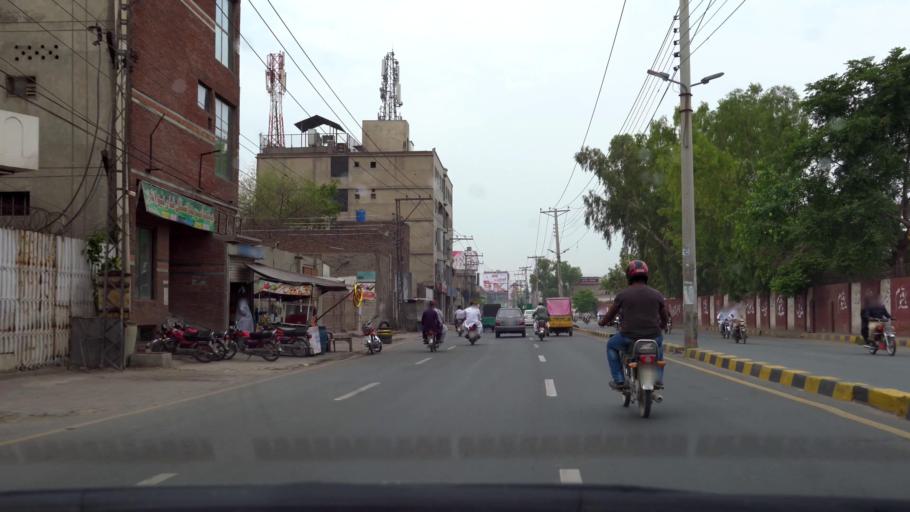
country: PK
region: Punjab
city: Faisalabad
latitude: 31.4256
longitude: 73.0721
